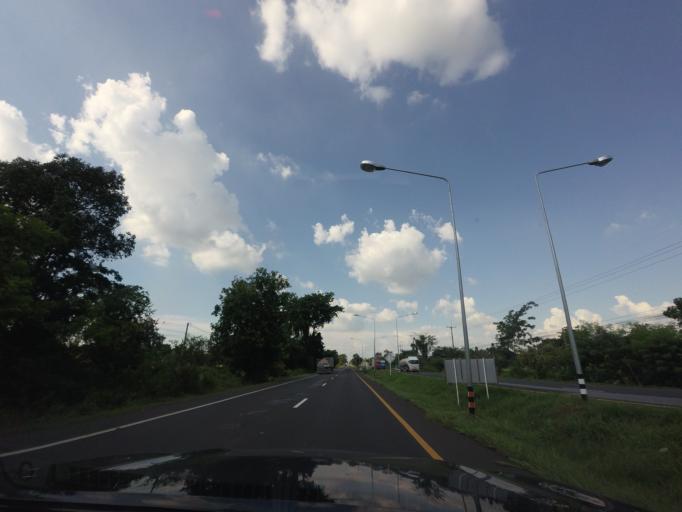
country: TH
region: Nakhon Ratchasima
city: Bua Lai
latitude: 15.7051
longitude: 102.5857
